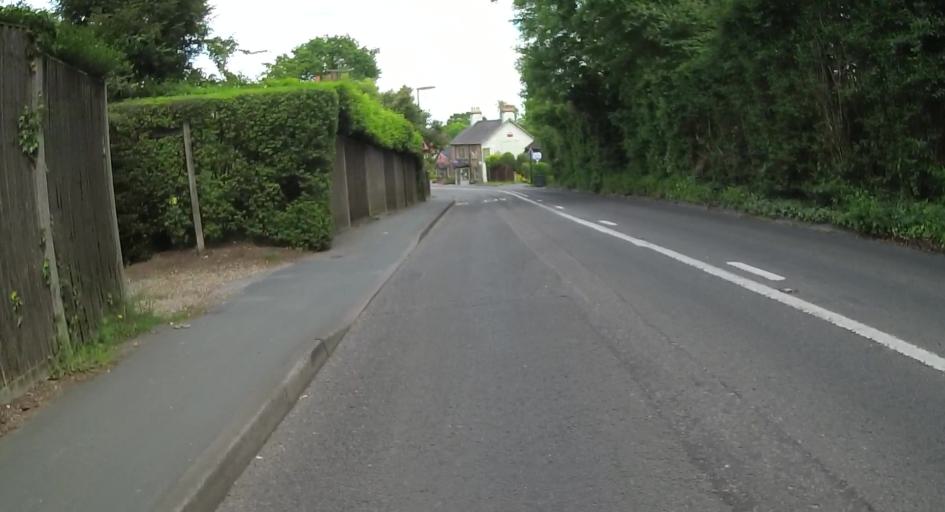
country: GB
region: England
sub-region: Surrey
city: Hale
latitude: 51.2376
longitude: -0.7931
